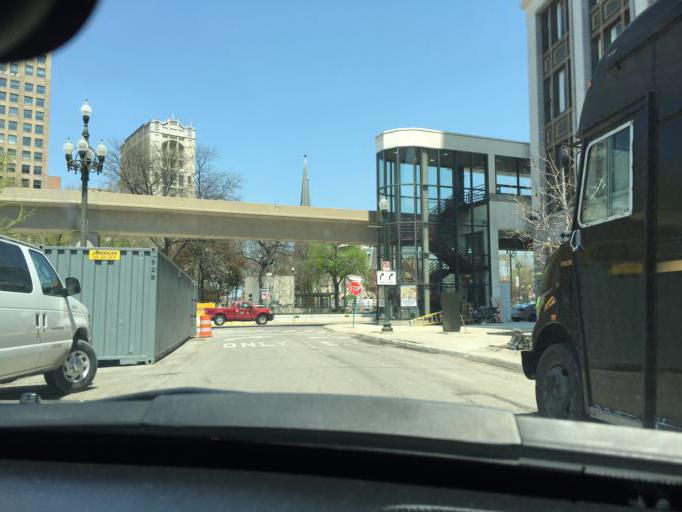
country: US
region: Michigan
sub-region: Wayne County
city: Detroit
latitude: 42.3355
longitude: -83.0508
